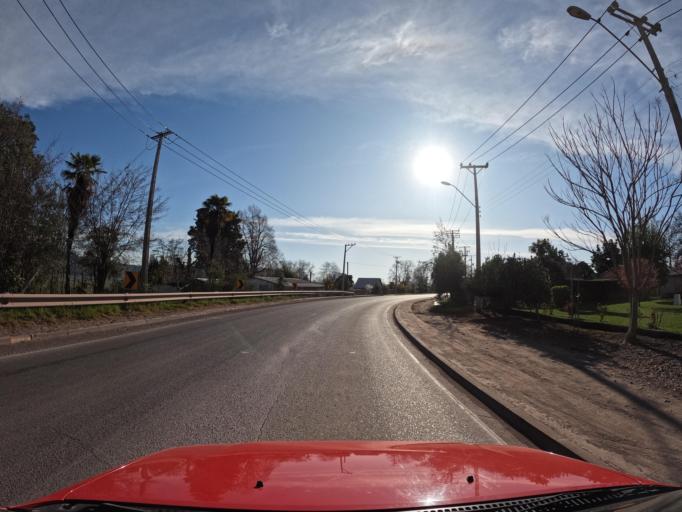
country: CL
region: Maule
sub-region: Provincia de Curico
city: Teno
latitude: -34.9620
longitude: -70.9674
